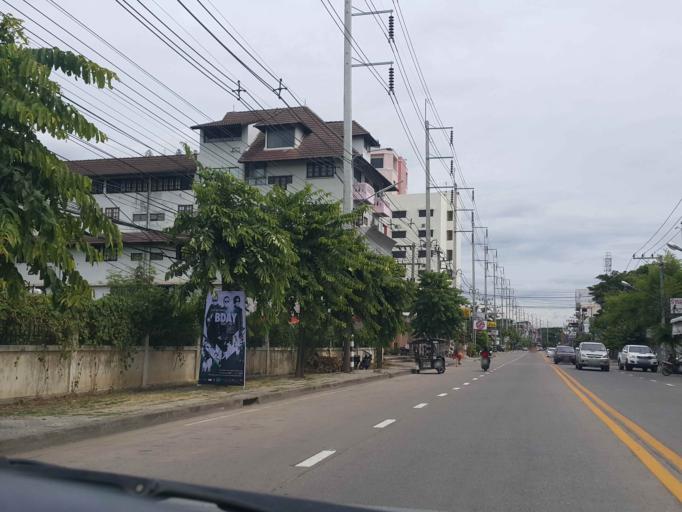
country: TH
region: Chiang Mai
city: Chiang Mai
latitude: 18.7654
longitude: 99.0003
